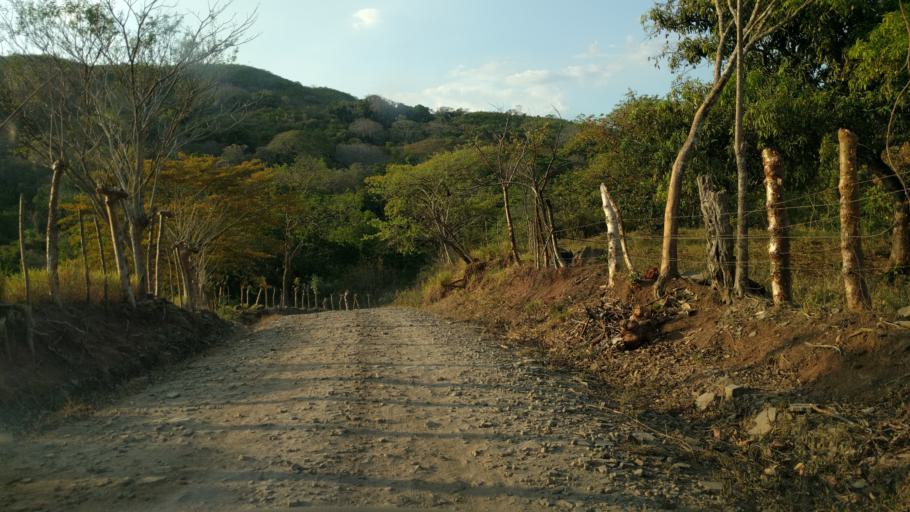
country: CR
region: Puntarenas
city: Esparza
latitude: 10.0179
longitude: -84.6960
